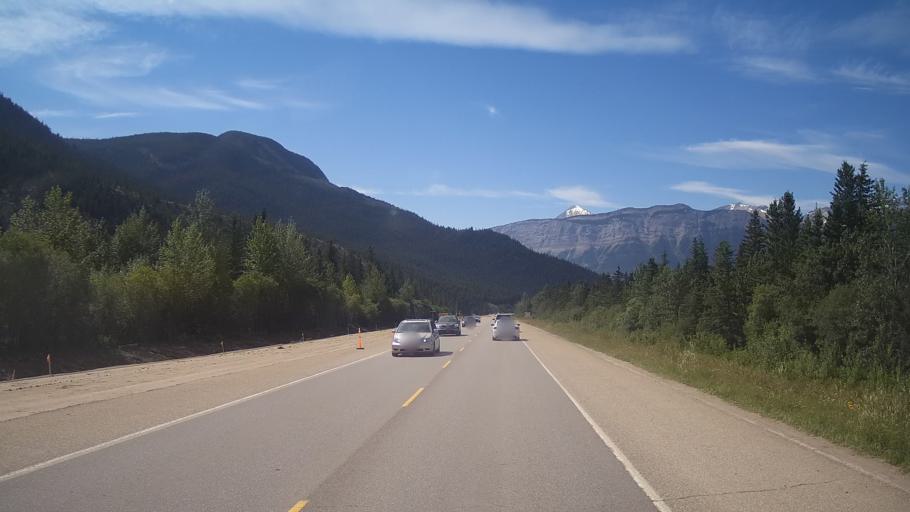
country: CA
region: Alberta
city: Jasper Park Lodge
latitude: 53.0614
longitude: -118.0663
